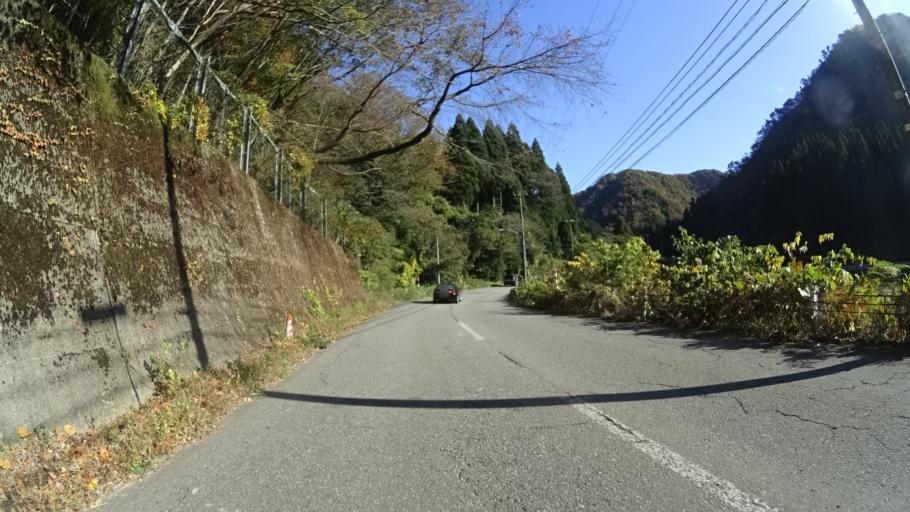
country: JP
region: Ishikawa
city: Tsurugi-asahimachi
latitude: 36.3729
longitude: 136.5624
